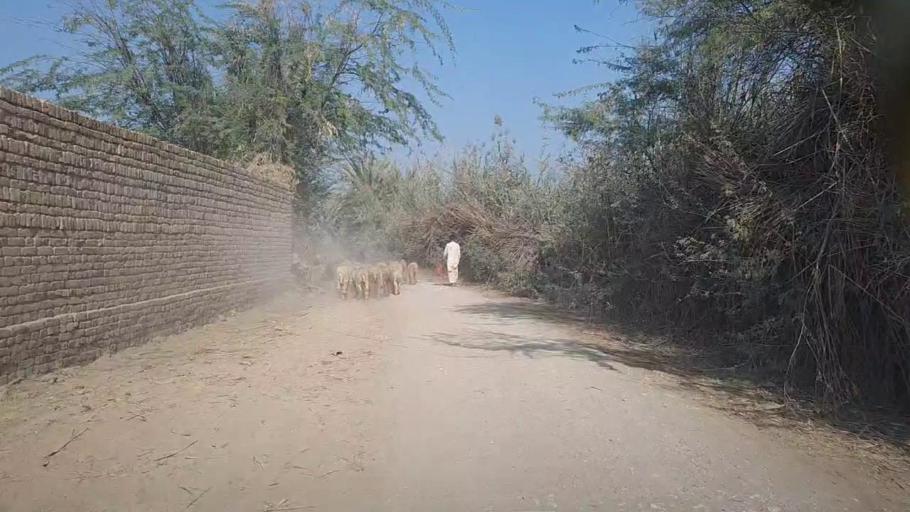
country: PK
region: Sindh
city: Karaundi
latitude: 26.9790
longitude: 68.4488
